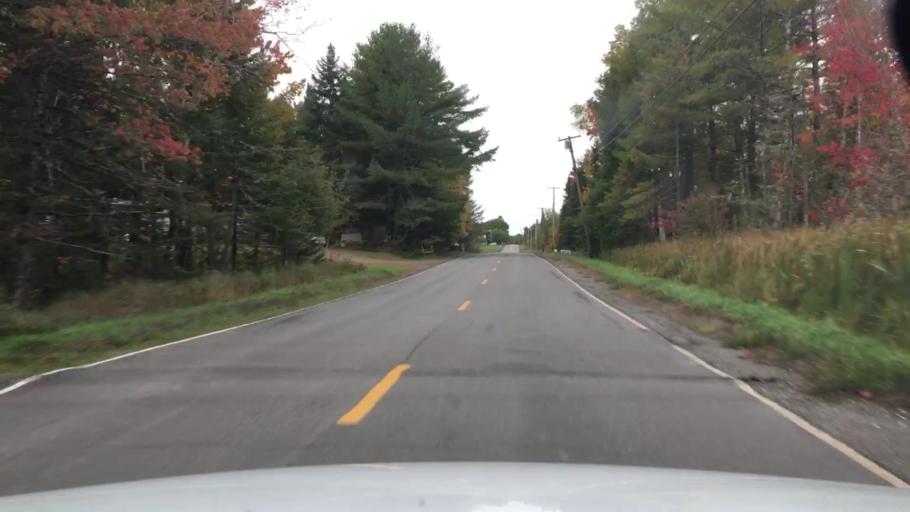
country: US
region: Maine
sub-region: Penobscot County
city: Hudson
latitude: 44.9884
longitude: -68.7613
